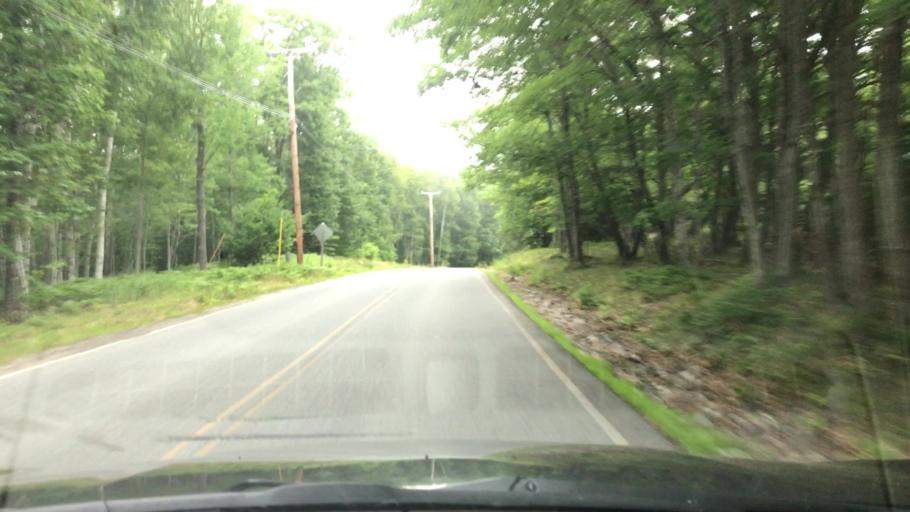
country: US
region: Maine
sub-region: Hancock County
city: Bar Harbor
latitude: 44.3404
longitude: -68.1806
